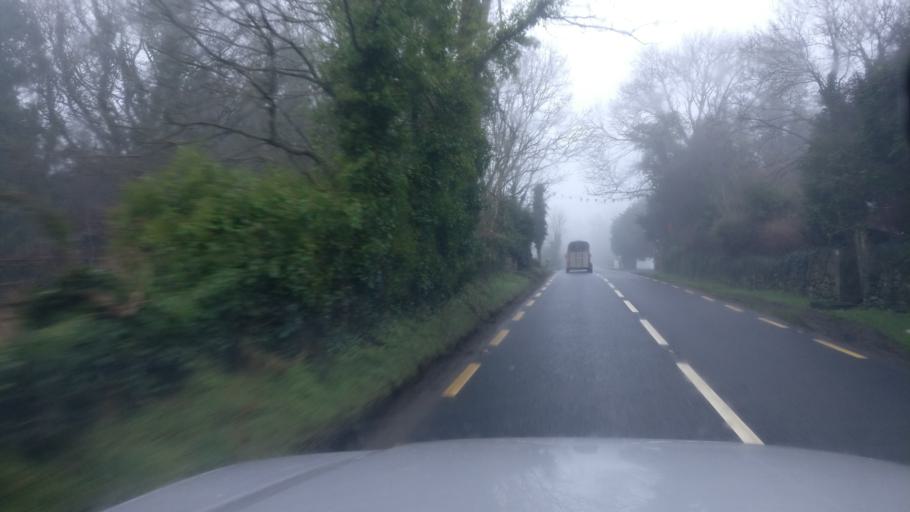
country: IE
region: Connaught
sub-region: County Galway
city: Loughrea
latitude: 53.1569
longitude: -8.6883
